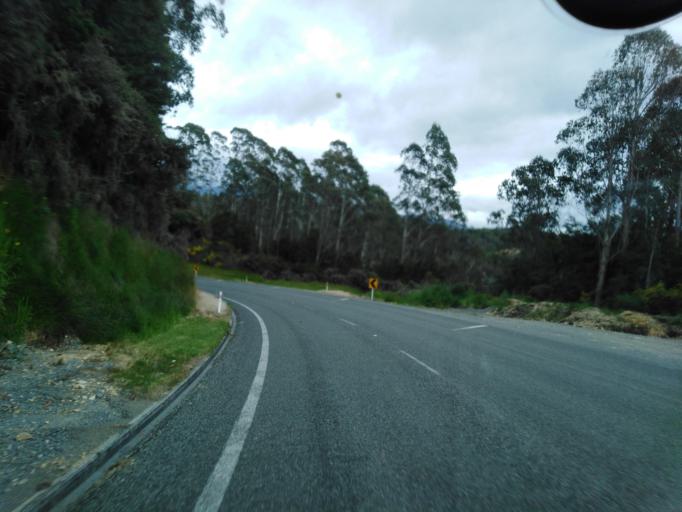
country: NZ
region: Tasman
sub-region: Tasman District
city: Wakefield
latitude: -41.6288
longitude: 172.7011
